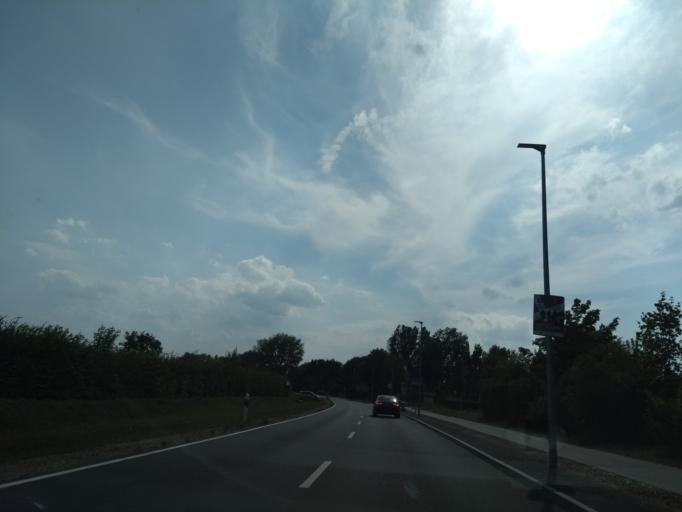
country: DE
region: Brandenburg
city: Lubbenau
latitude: 51.8573
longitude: 13.9638
